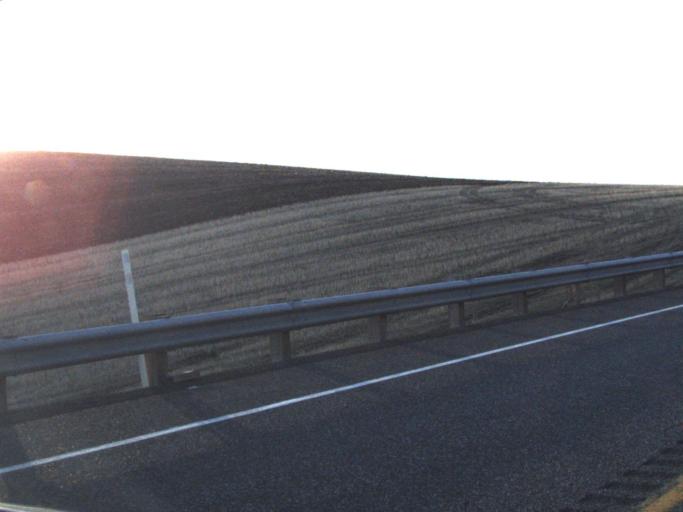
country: US
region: Washington
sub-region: Garfield County
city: Pomeroy
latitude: 46.7209
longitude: -117.7685
